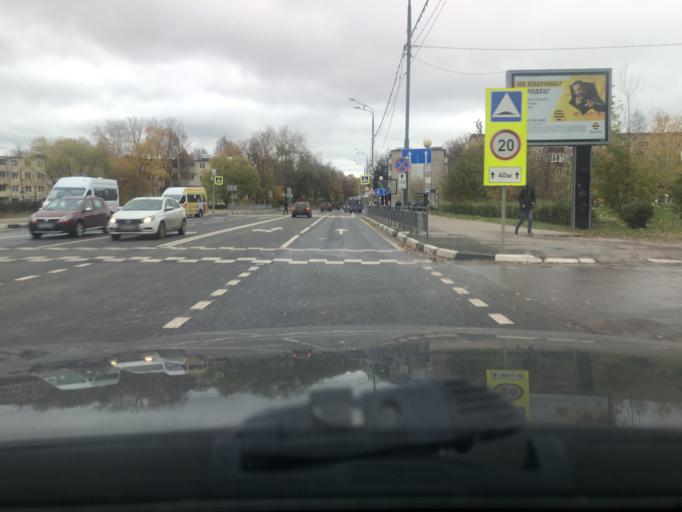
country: RU
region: Moskovskaya
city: Sergiyev Posad
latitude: 56.3218
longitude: 38.1370
